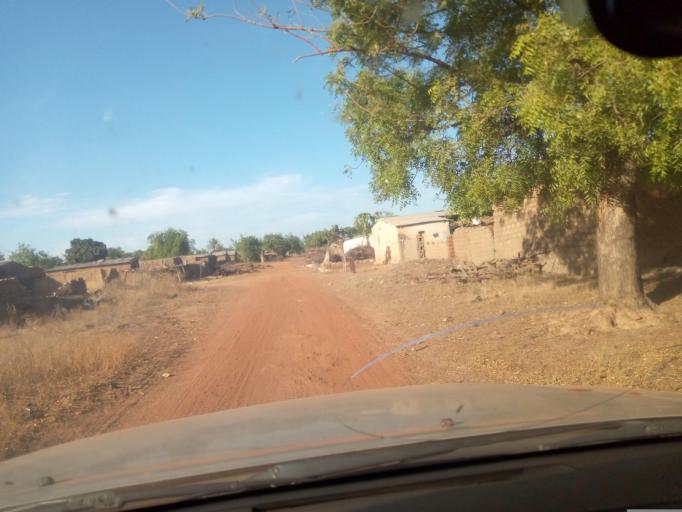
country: ML
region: Sikasso
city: Sikasso
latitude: 11.4828
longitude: -5.4813
